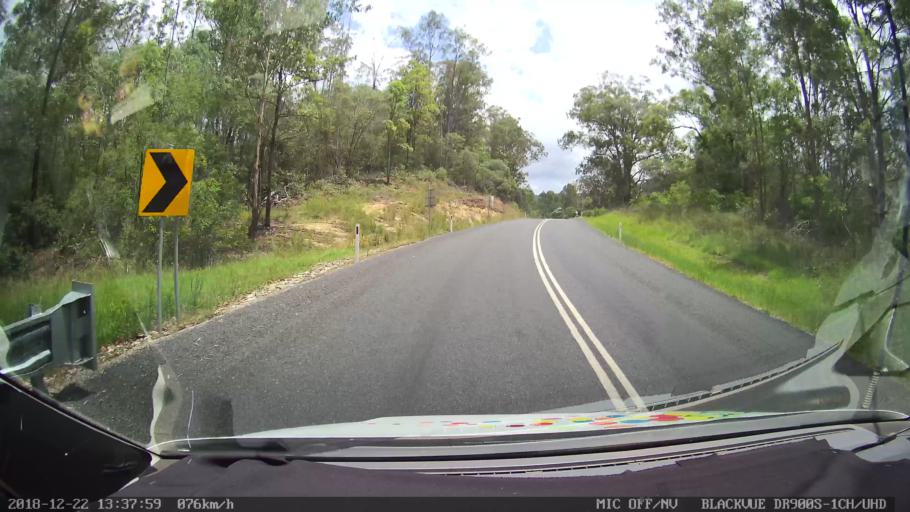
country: AU
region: New South Wales
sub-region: Clarence Valley
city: Coutts Crossing
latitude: -29.8955
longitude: 152.7895
